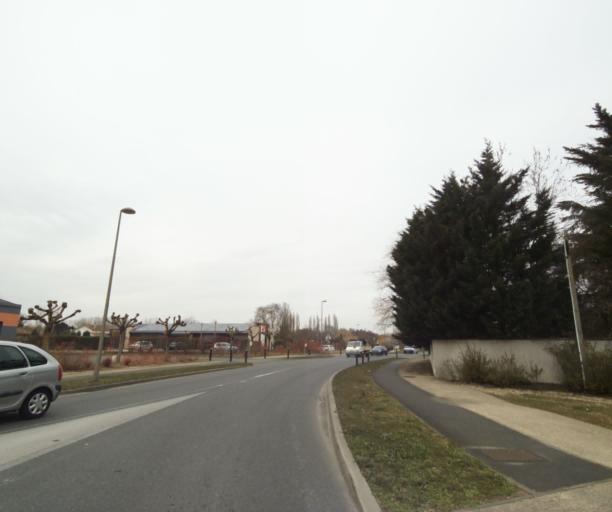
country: FR
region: Poitou-Charentes
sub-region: Departement des Deux-Sevres
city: Bessines
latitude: 46.3167
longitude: -0.4929
